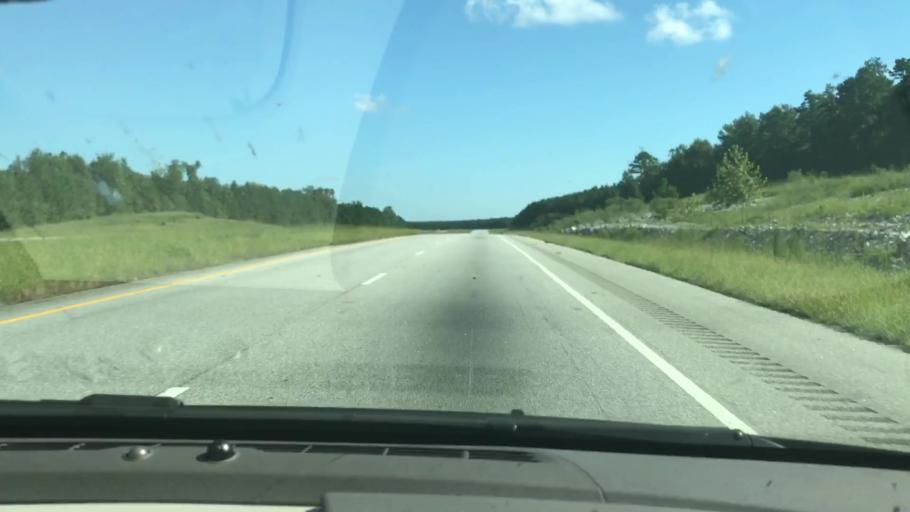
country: US
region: Alabama
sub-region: Russell County
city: Ladonia
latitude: 32.2051
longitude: -85.1732
